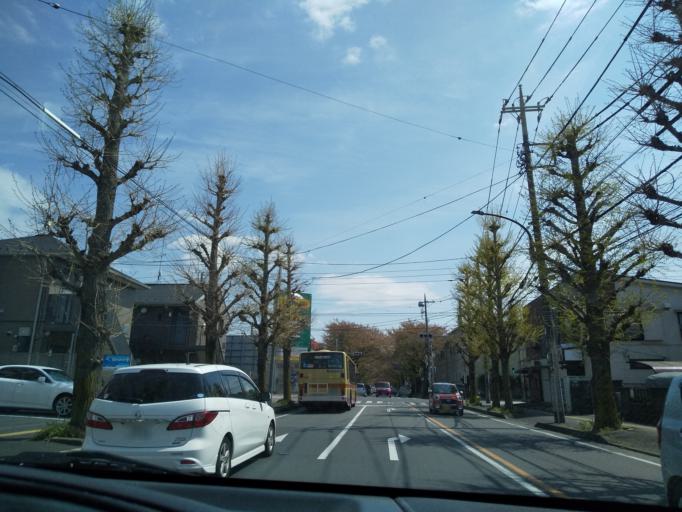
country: JP
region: Tokyo
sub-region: Machida-shi
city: Machida
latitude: 35.5611
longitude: 139.3828
